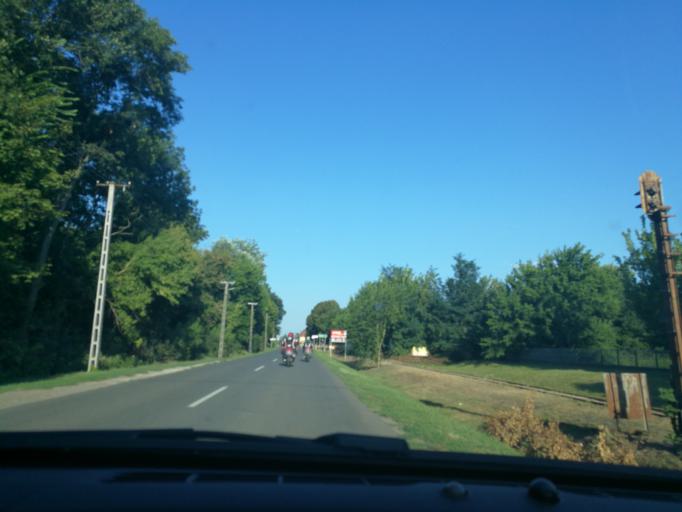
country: HU
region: Szabolcs-Szatmar-Bereg
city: Tiszabercel
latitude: 48.1694
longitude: 21.5588
